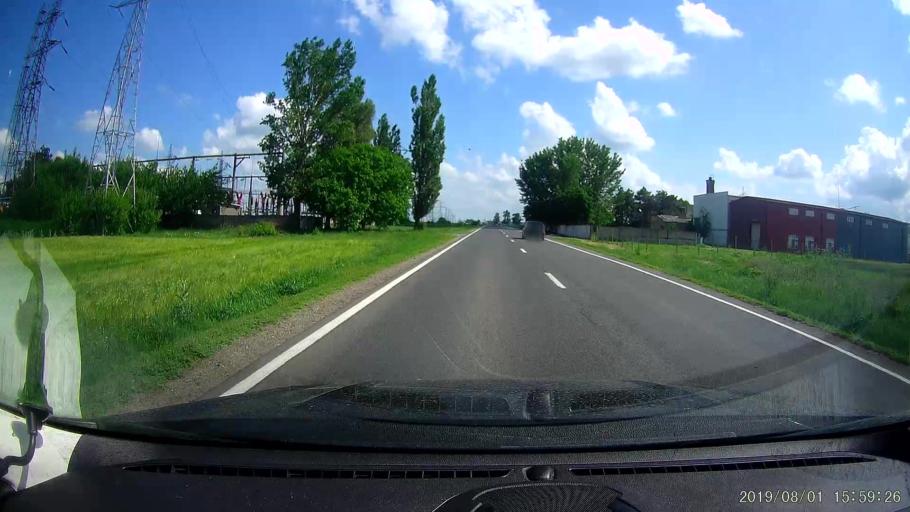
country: RO
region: Ialomita
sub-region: Comuna Slobozia
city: Slobozia
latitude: 44.5487
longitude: 27.3833
